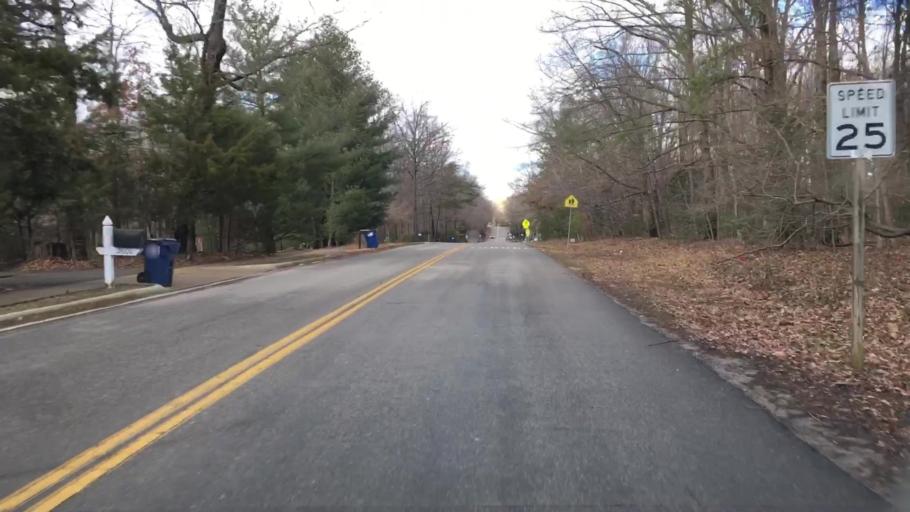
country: US
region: Virginia
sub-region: Chesterfield County
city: Bon Air
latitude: 37.5267
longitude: -77.6152
